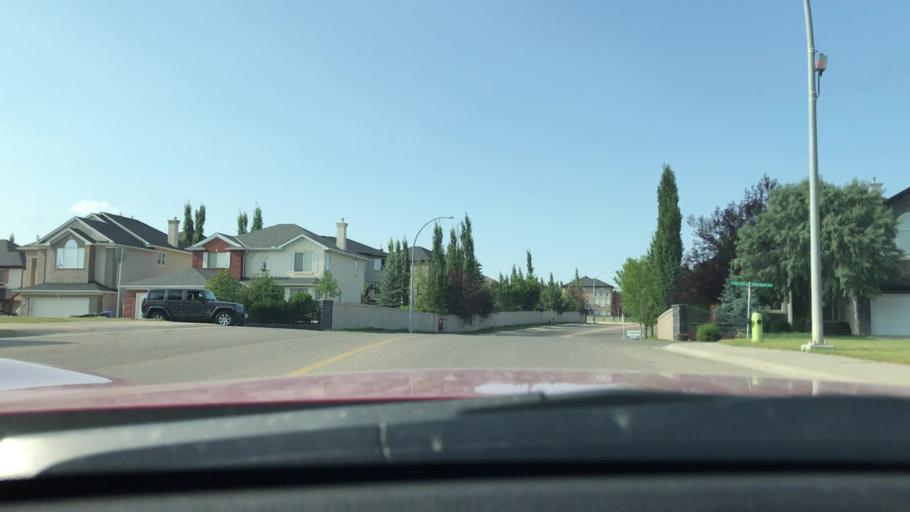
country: CA
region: Alberta
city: Calgary
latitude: 51.0288
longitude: -114.1821
